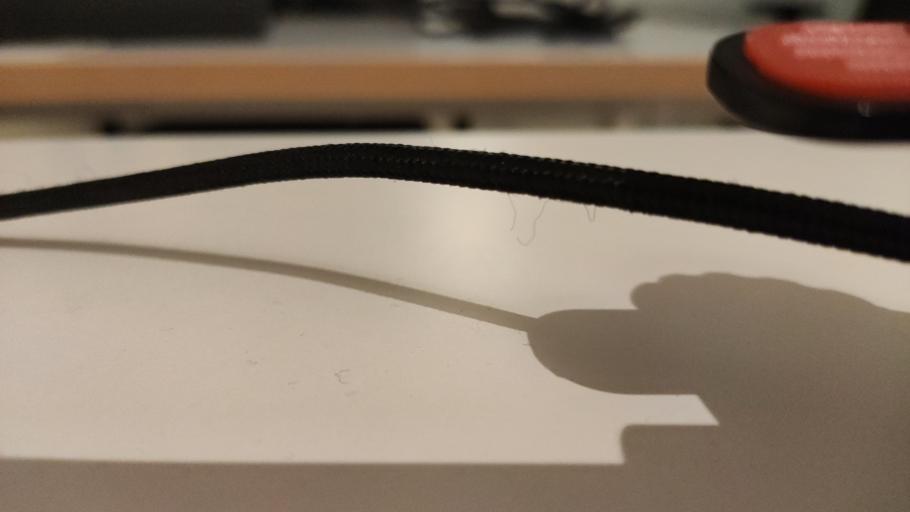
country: RU
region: Moskovskaya
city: Kurovskoye
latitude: 55.5949
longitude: 38.9238
